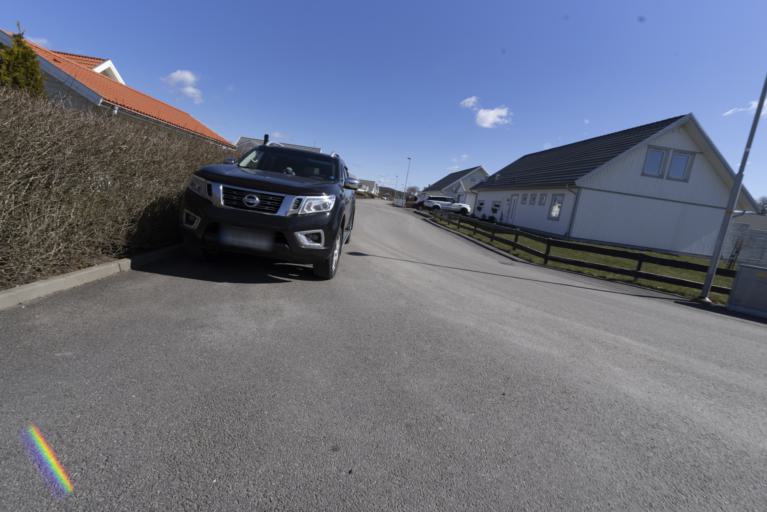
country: SE
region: Halland
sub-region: Varbergs Kommun
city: Varberg
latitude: 57.1547
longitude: 12.2551
